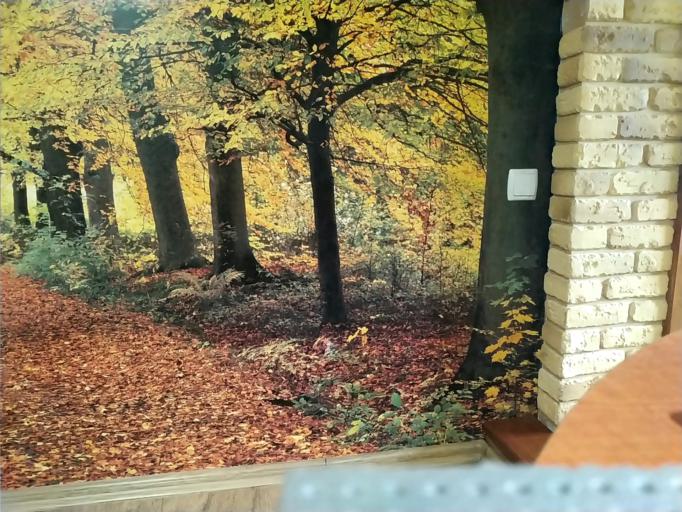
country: RU
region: Tverskaya
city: Kalashnikovo
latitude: 57.2732
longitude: 35.2417
